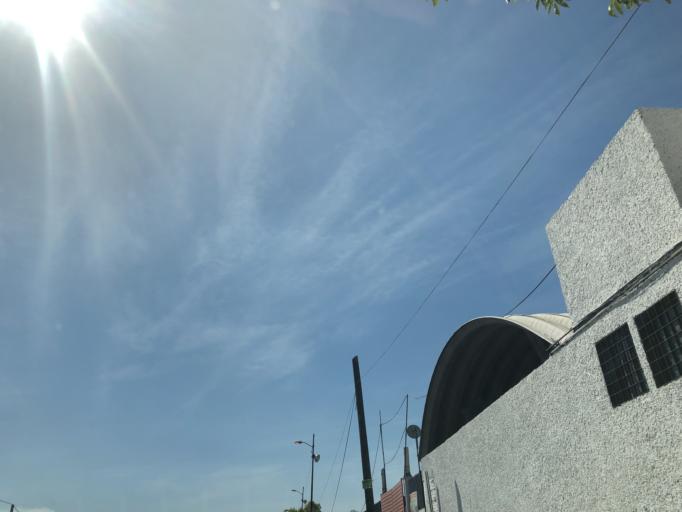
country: MX
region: Mexico
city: Ciudad Nezahualcoyotl
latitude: 19.3826
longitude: -99.0397
